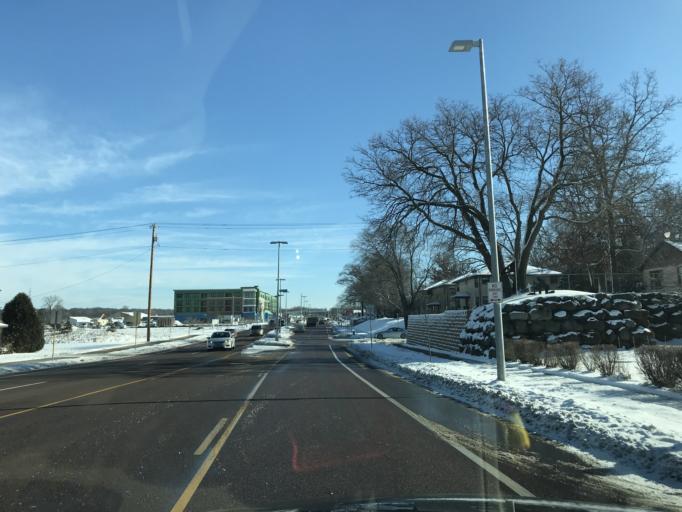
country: US
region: Wisconsin
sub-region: Dane County
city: Monona
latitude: 43.0837
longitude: -89.3213
